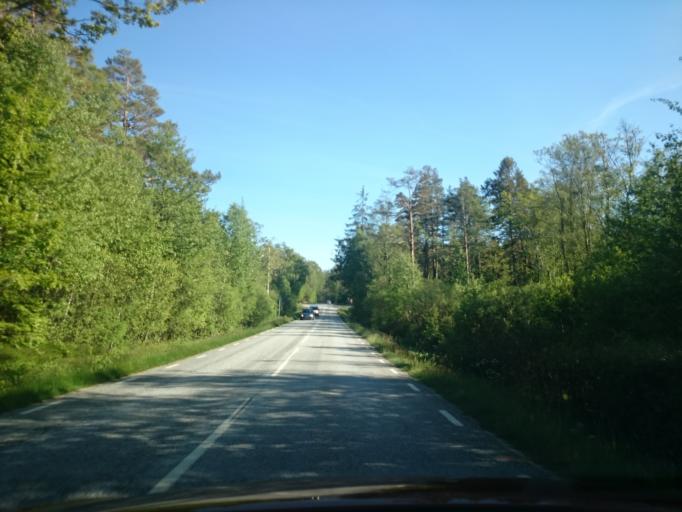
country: SE
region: Vaestra Goetaland
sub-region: Lysekils Kommun
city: Lysekil
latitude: 58.2756
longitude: 11.5314
